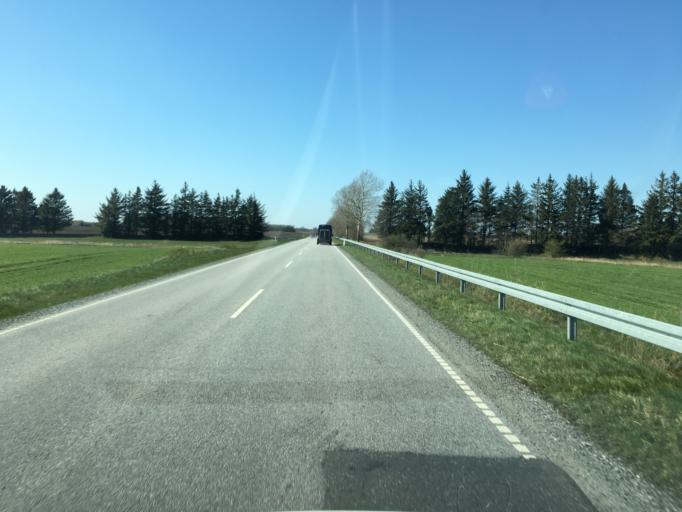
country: DK
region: South Denmark
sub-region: Aabenraa Kommune
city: Tinglev
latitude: 54.9506
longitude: 9.3454
